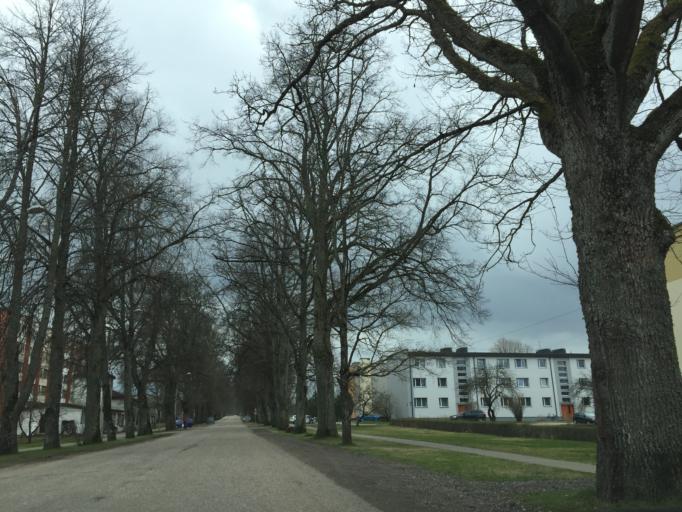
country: LV
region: Priekuli
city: Priekuli
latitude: 57.3540
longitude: 25.3324
